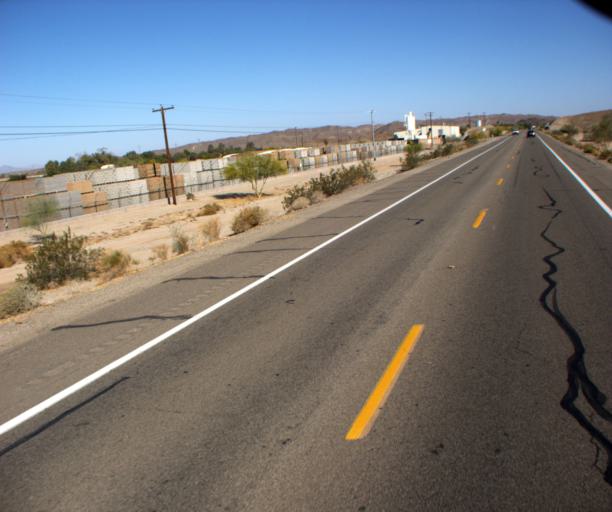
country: US
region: Arizona
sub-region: Yuma County
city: Fortuna Foothills
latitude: 32.7322
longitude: -114.4231
